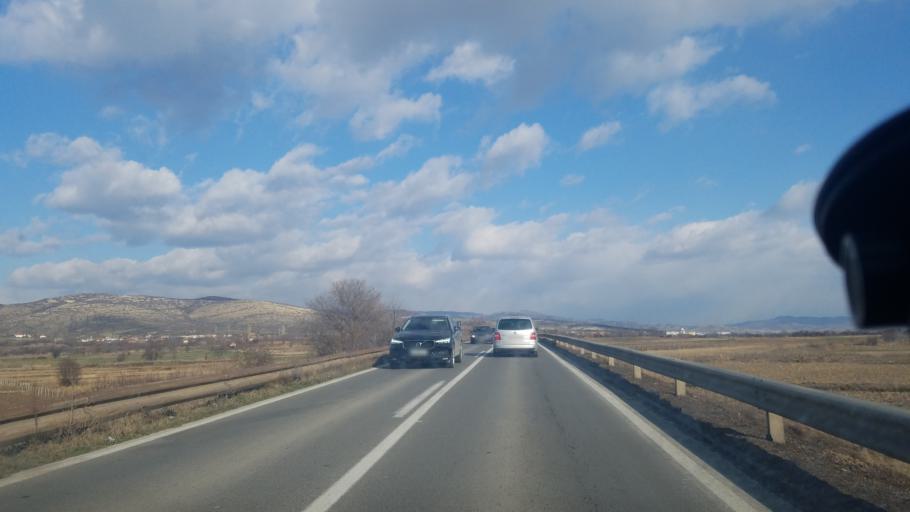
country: MK
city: Obleshevo
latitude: 41.8936
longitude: 22.3531
